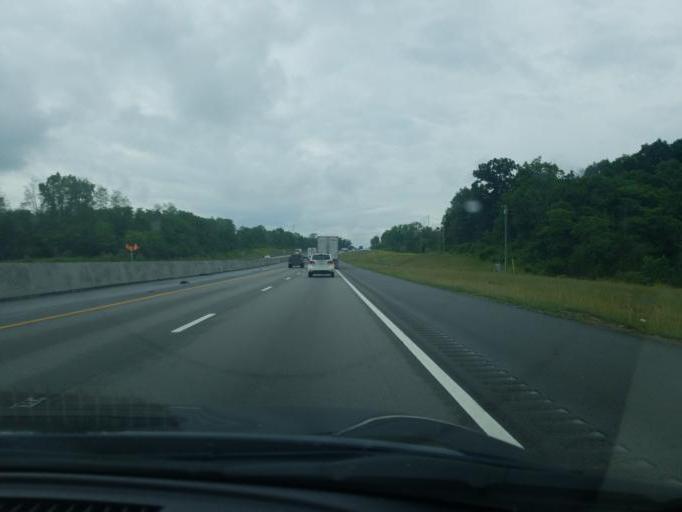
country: US
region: Ohio
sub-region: Warren County
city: Morrow
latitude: 39.4180
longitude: -84.1074
